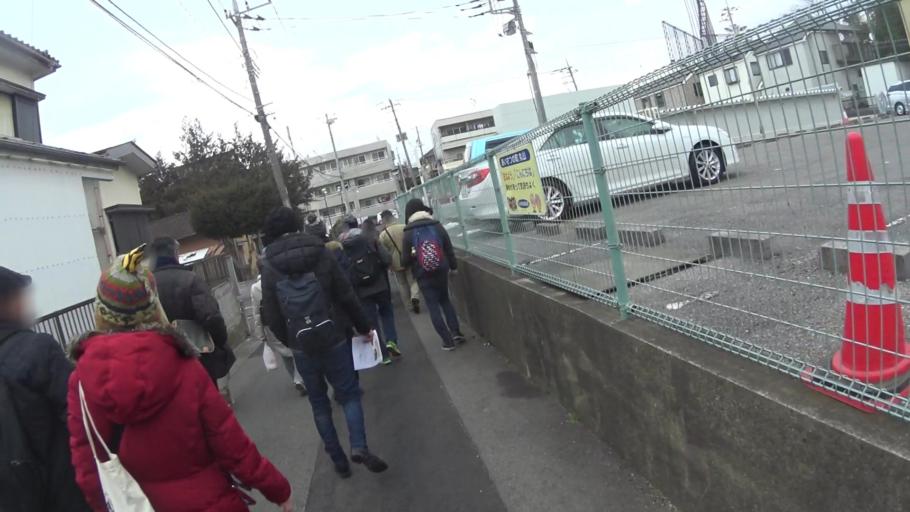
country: JP
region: Chiba
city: Funabashi
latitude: 35.7471
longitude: 139.9936
